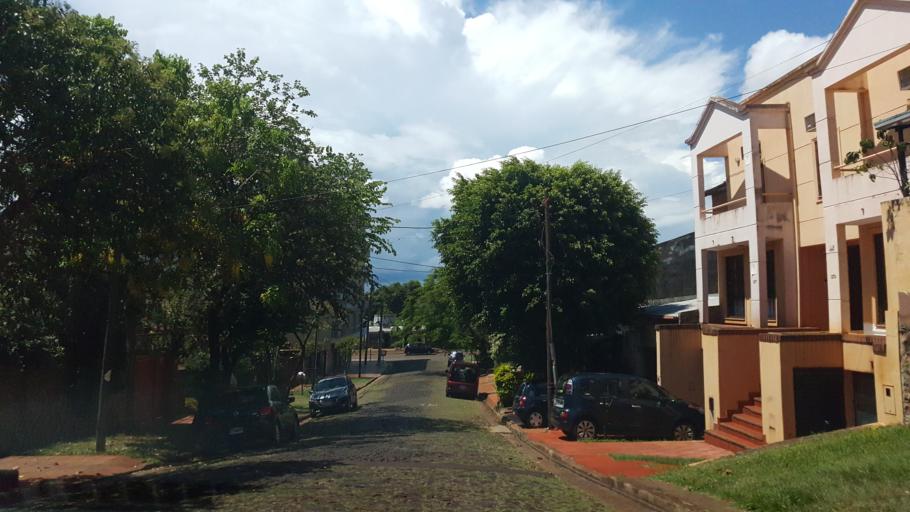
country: AR
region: Misiones
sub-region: Departamento de Capital
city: Posadas
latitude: -27.3612
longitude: -55.9027
